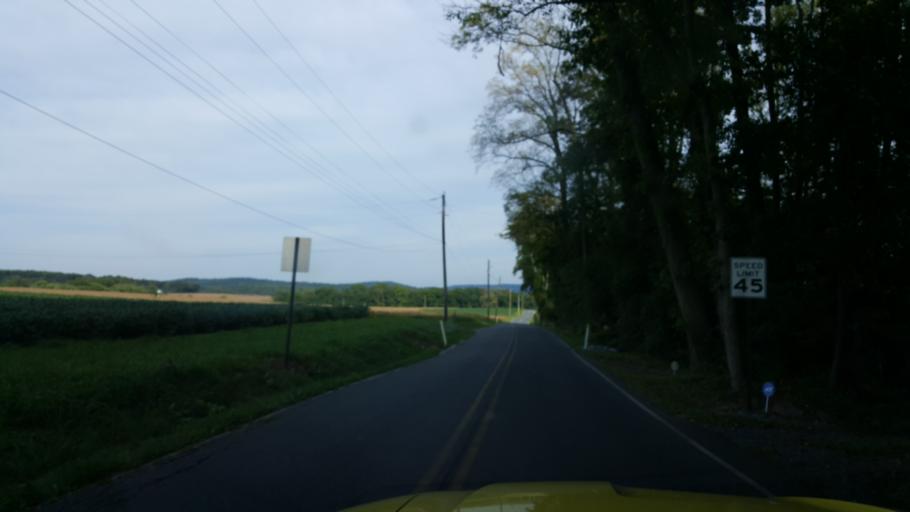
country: US
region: Pennsylvania
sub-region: Lebanon County
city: Campbelltown
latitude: 40.2381
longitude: -76.5738
